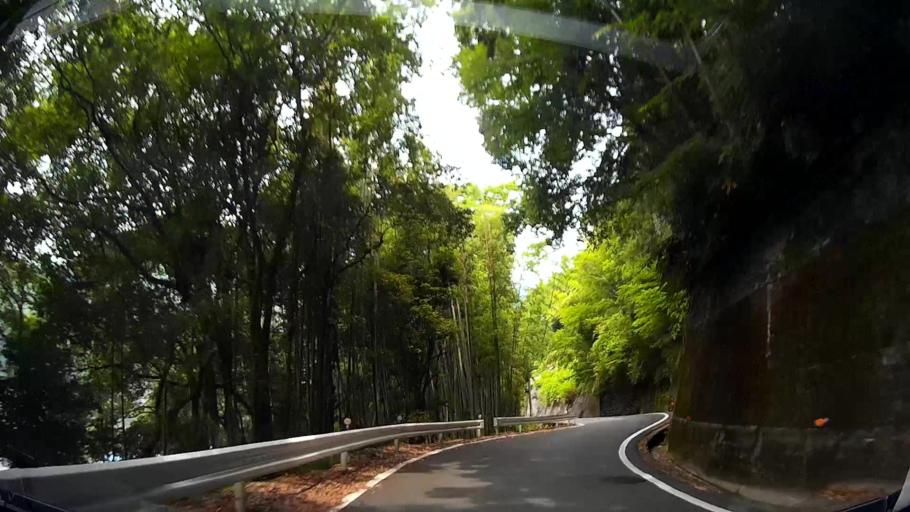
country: JP
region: Shizuoka
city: Hamakita
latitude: 35.0797
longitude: 137.7967
